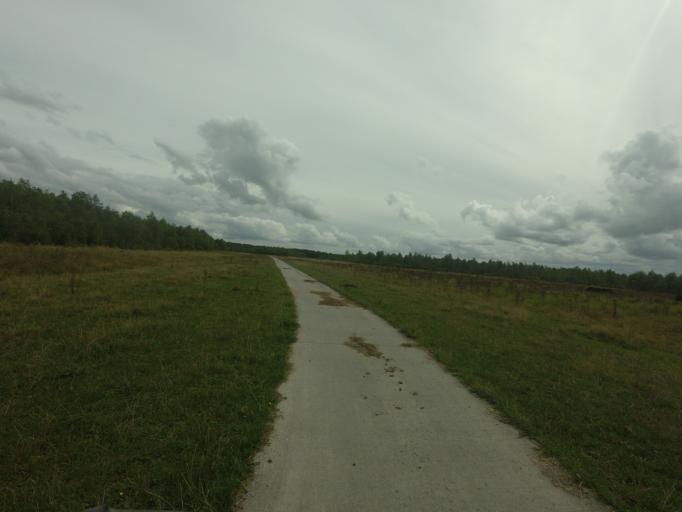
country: NL
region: Drenthe
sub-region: Gemeente Westerveld
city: Dwingeloo
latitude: 52.9847
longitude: 6.3803
